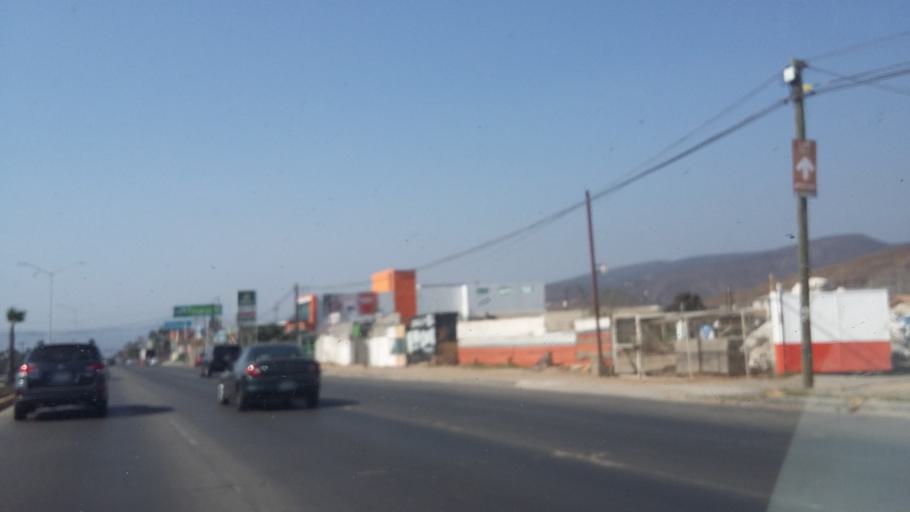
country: MX
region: Baja California
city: Rodolfo Sanchez Taboada
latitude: 31.7921
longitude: -116.5929
